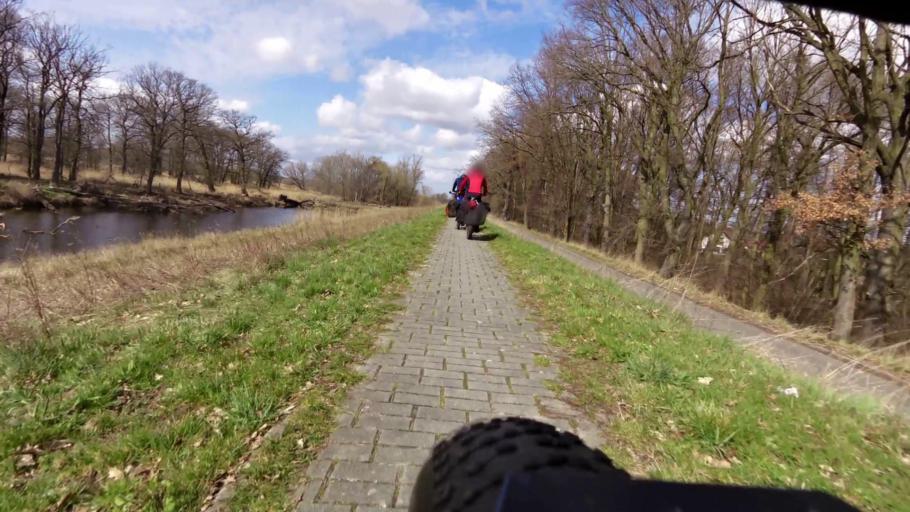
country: PL
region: Lubusz
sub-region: Powiat slubicki
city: Slubice
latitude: 52.3739
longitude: 14.5595
